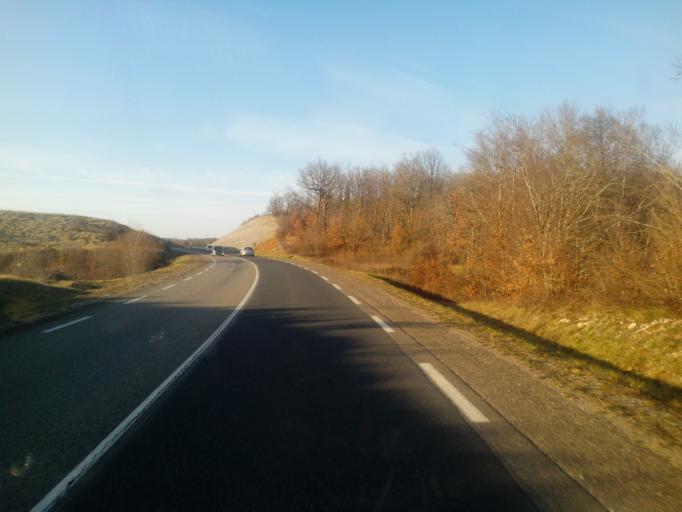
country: FR
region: Limousin
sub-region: Departement de la Correze
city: Brive-la-Gaillarde
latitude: 45.0345
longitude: 1.5075
